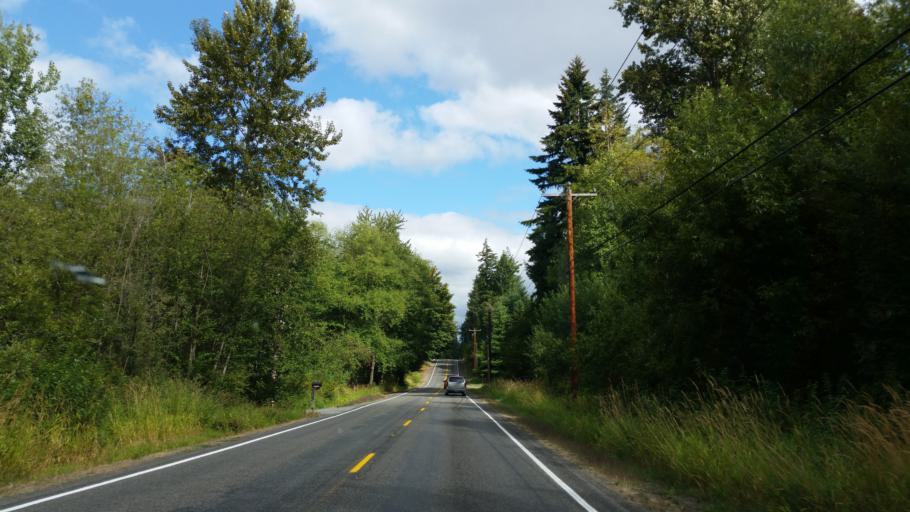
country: US
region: Washington
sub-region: Pierce County
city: Bonney Lake
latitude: 47.2467
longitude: -122.1584
